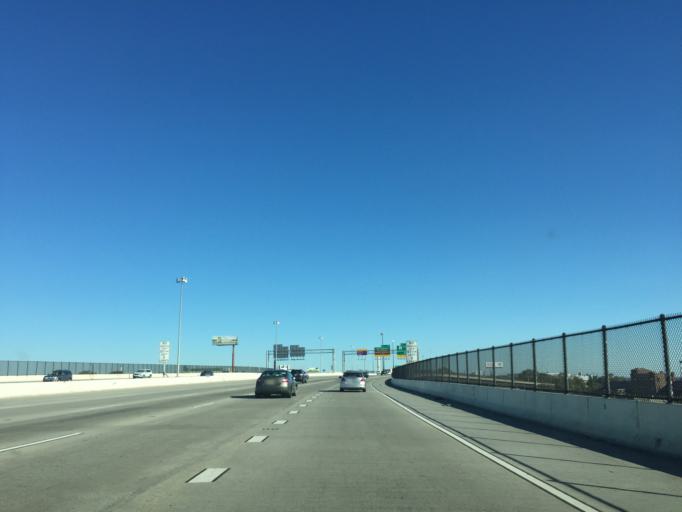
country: US
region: Maryland
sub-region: City of Baltimore
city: Baltimore
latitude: 39.2669
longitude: -76.6201
